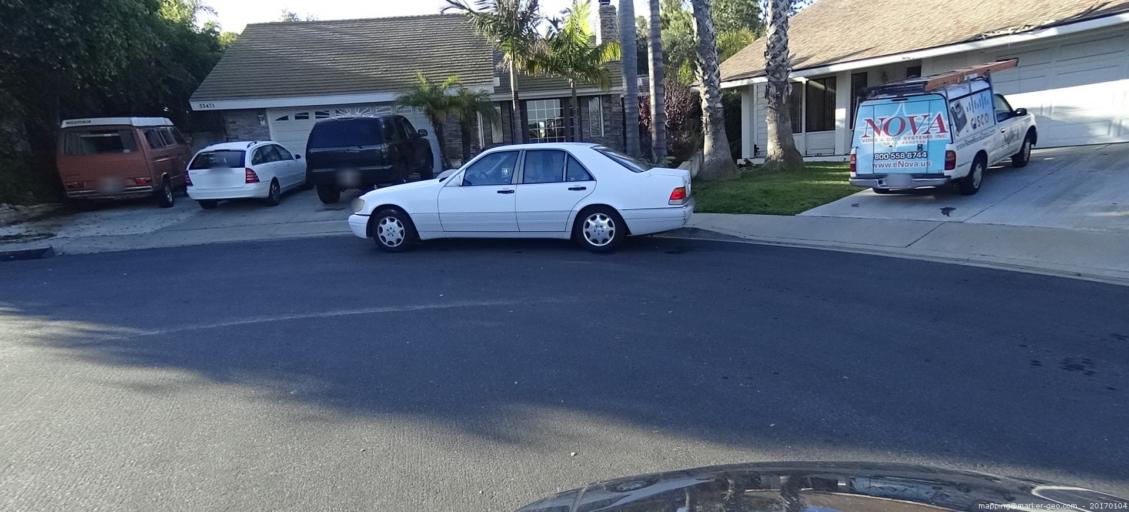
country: US
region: California
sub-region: Orange County
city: Dana Point
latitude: 33.4770
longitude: -117.7038
